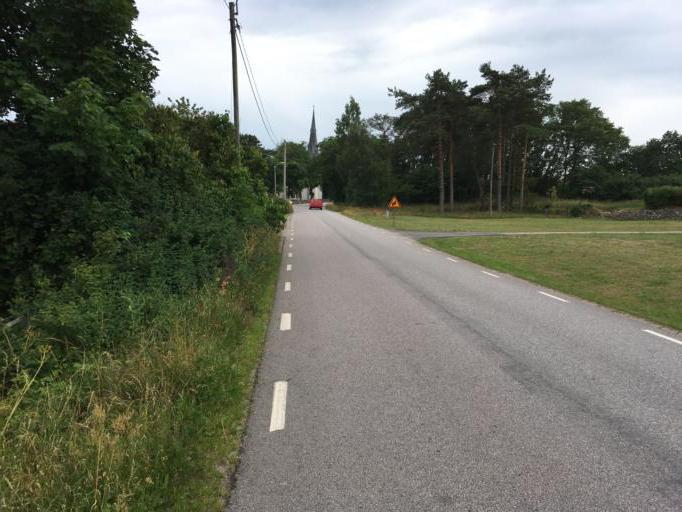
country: SE
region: Blekinge
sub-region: Karlskrona Kommun
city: Sturko
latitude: 56.0905
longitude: 15.6957
